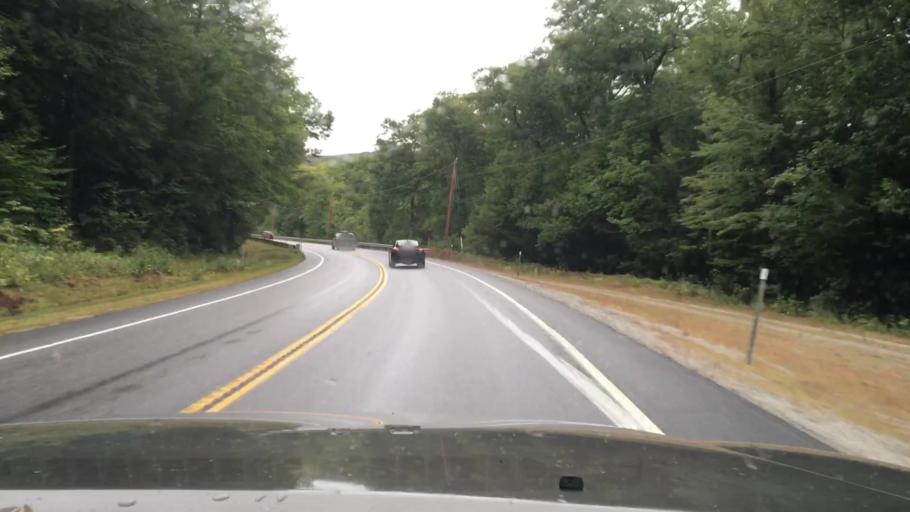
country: US
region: New Hampshire
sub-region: Hillsborough County
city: Antrim
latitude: 43.0745
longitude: -72.0401
